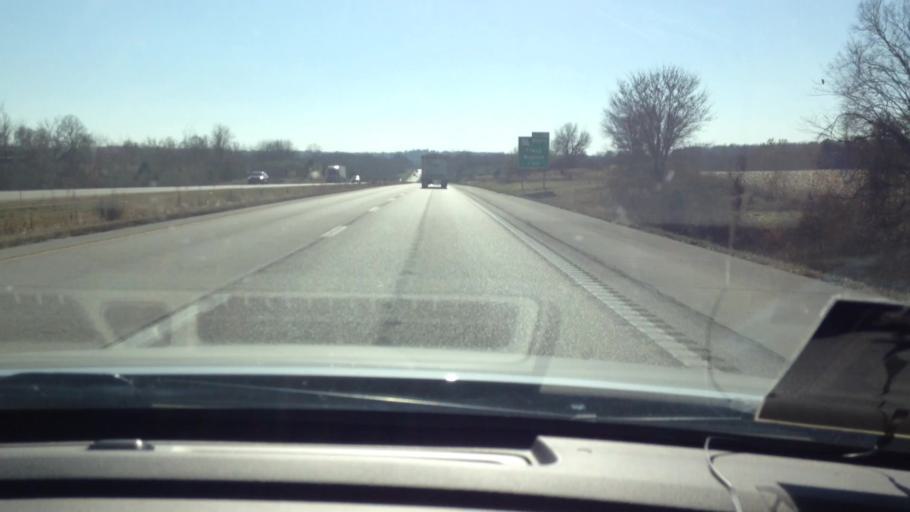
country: US
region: Missouri
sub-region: Platte County
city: Platte City
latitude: 39.4019
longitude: -94.7898
